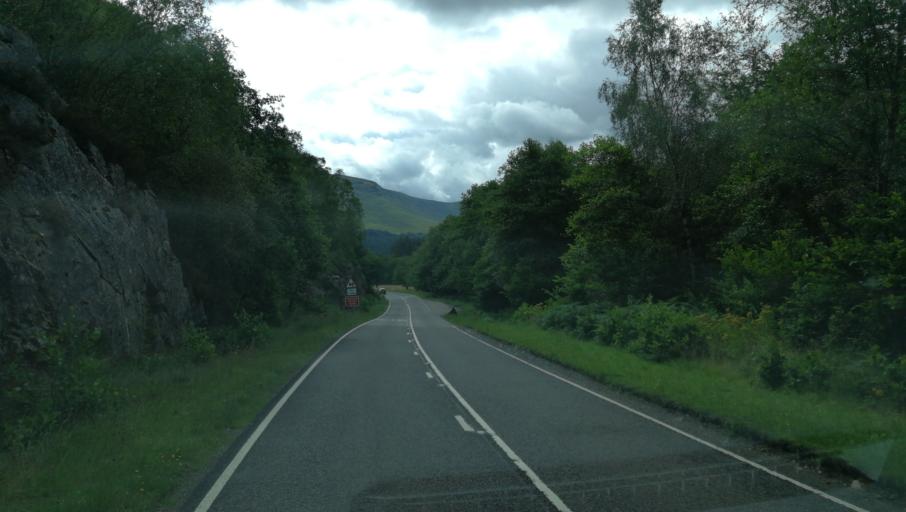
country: GB
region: Scotland
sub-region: Highland
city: Fort William
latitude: 56.8629
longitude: -5.4108
